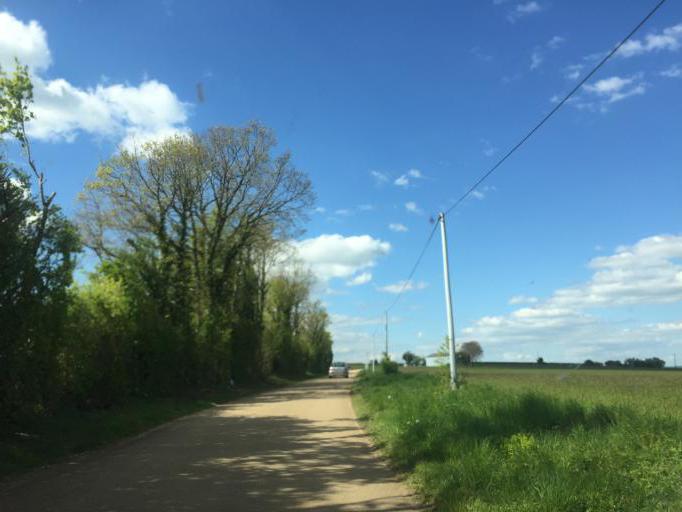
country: FR
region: Bourgogne
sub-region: Departement de l'Yonne
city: Fontenailles
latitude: 47.5683
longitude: 3.3442
